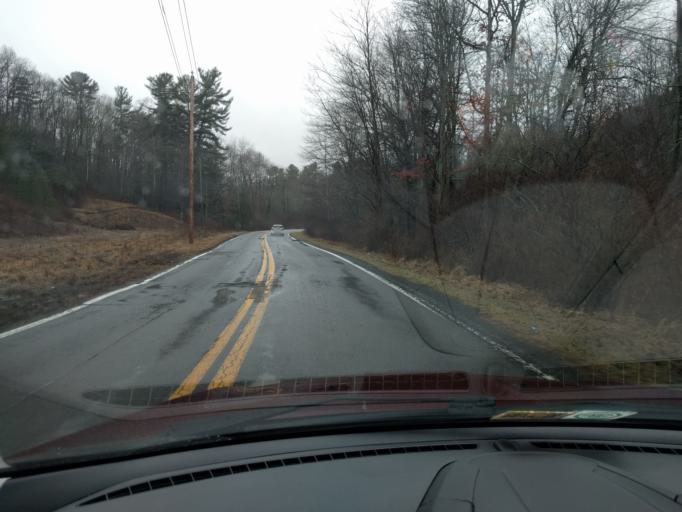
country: US
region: West Virginia
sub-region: Raleigh County
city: Beckley
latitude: 37.7963
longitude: -81.2034
